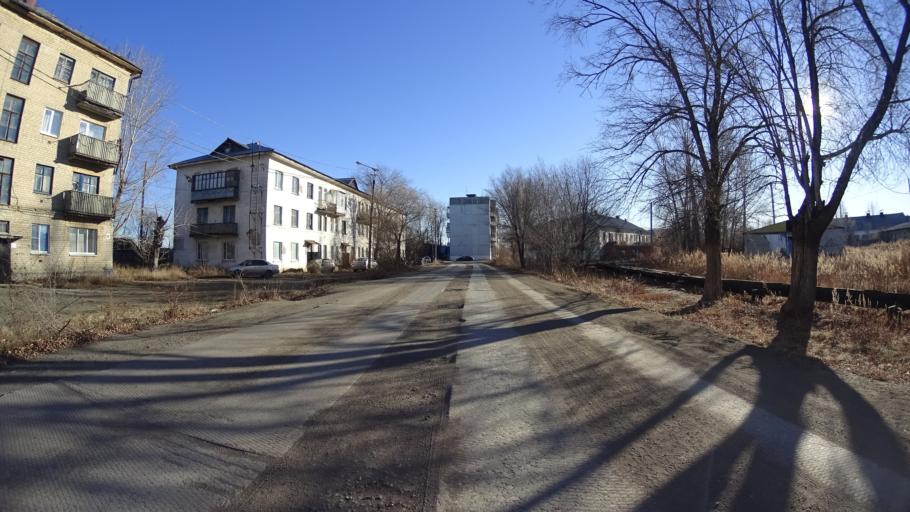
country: RU
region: Chelyabinsk
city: Troitsk
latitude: 54.1092
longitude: 61.5536
